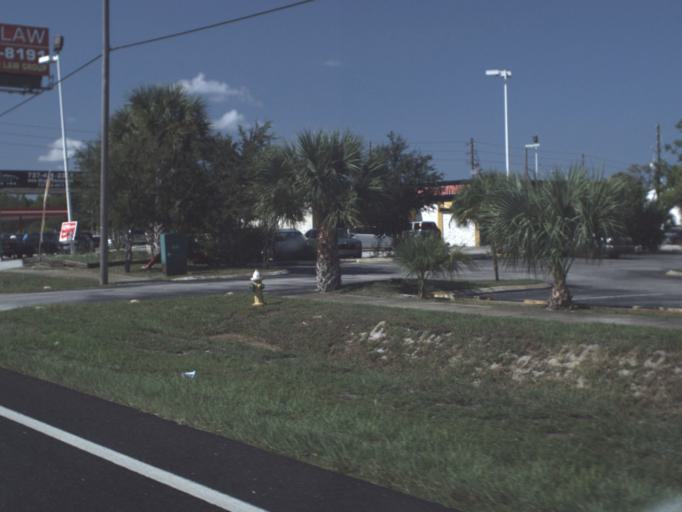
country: US
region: Florida
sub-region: Pinellas County
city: Tarpon Springs
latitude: 28.1240
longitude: -82.7402
